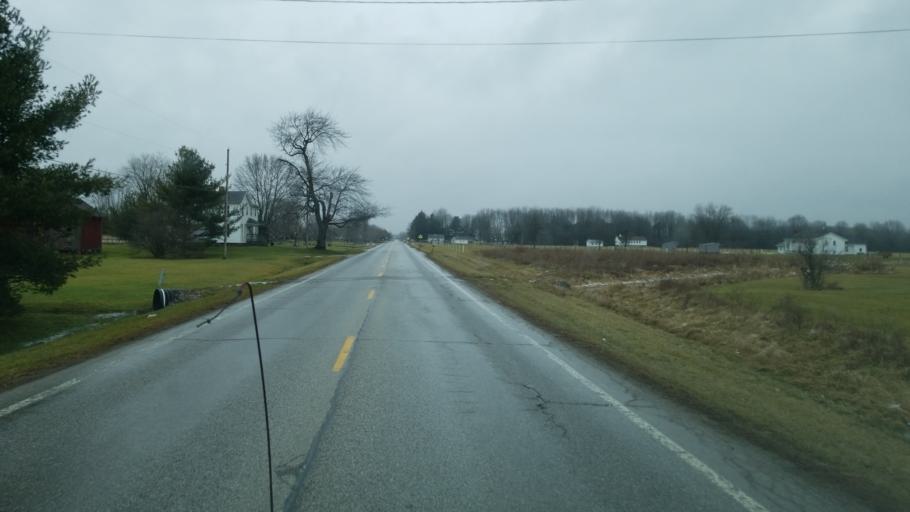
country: US
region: Ohio
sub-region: Geauga County
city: Middlefield
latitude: 41.4089
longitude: -80.9550
